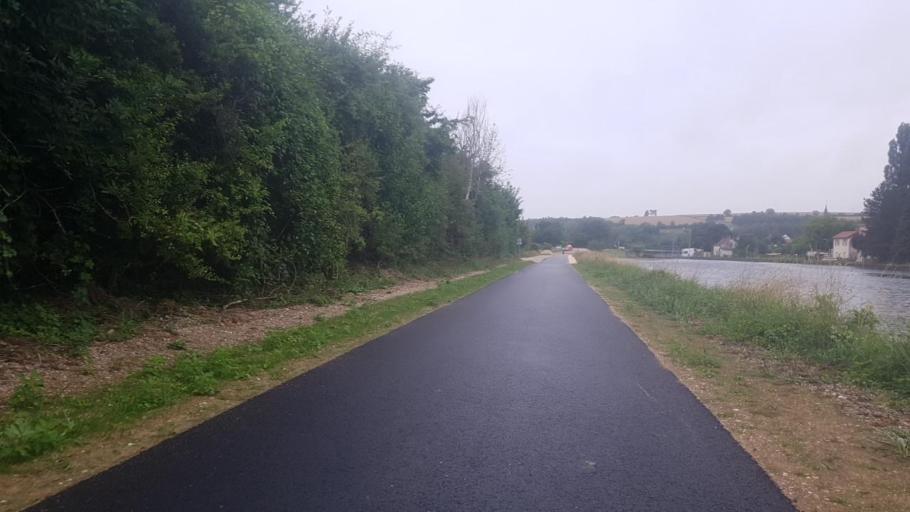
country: FR
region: Champagne-Ardenne
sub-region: Departement de la Marne
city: Vitry-le-Francois
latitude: 48.7883
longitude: 4.5342
